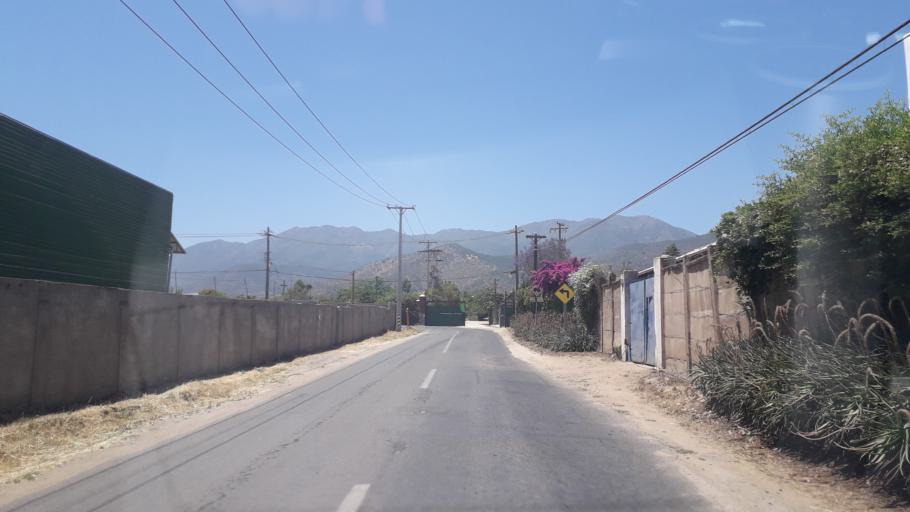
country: CL
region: Valparaiso
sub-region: Provincia de Quillota
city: Quillota
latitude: -32.9081
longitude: -71.2189
